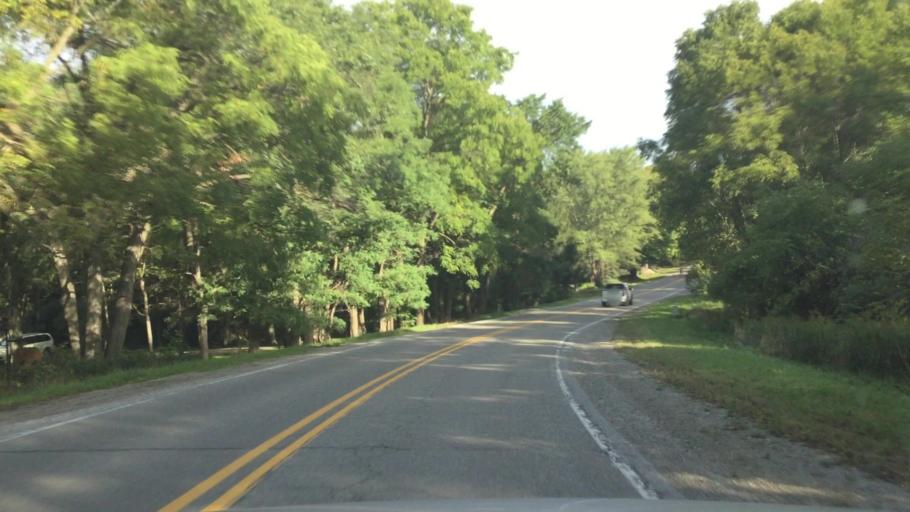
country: US
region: Michigan
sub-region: Livingston County
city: Howell
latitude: 42.5646
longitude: -83.8927
